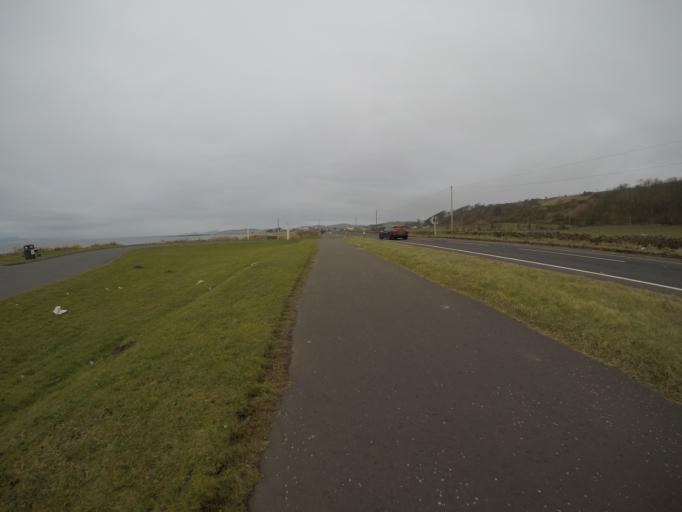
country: GB
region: Scotland
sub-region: North Ayrshire
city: West Kilbride
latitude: 55.6713
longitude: -4.8472
